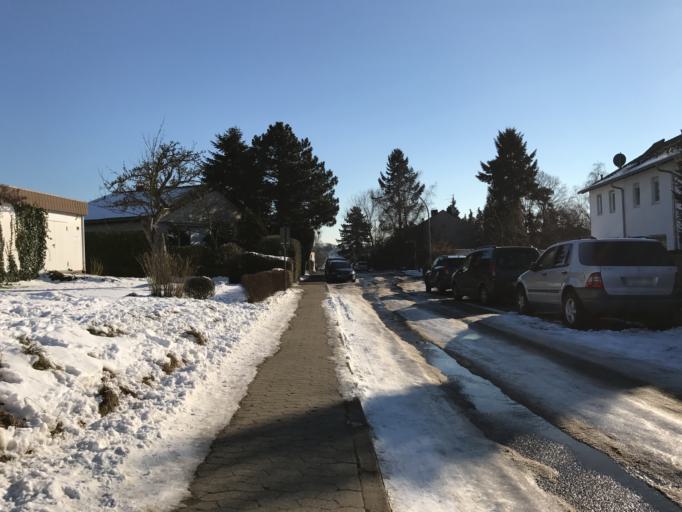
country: DE
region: Hesse
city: Eppstein
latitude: 50.1112
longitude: 8.3954
